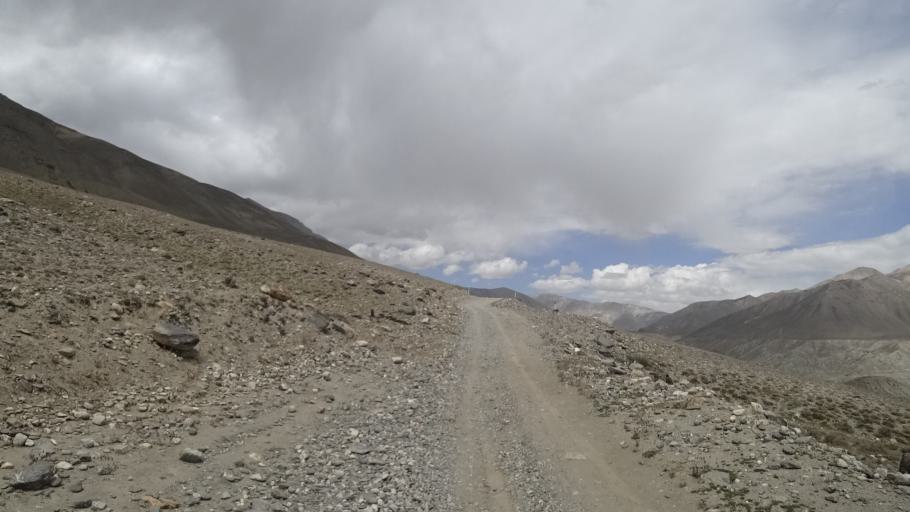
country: AF
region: Badakhshan
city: Khandud
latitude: 37.1409
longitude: 72.7376
